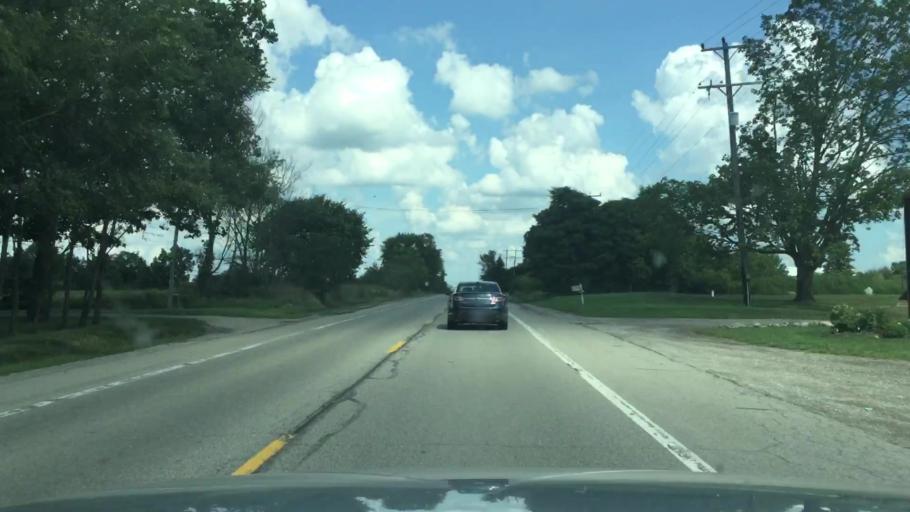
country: US
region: Michigan
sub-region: Washtenaw County
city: Saline
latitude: 42.1493
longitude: -83.8233
